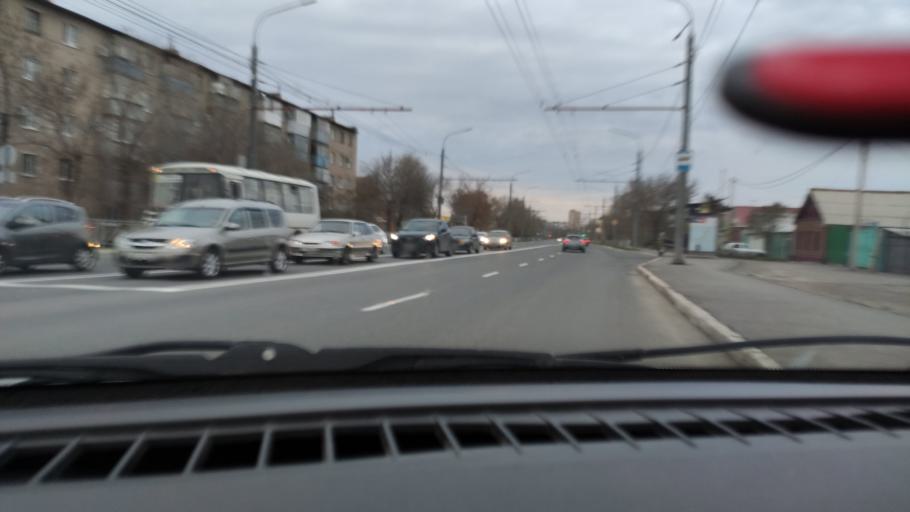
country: RU
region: Orenburg
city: Orenburg
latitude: 51.7810
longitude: 55.1143
